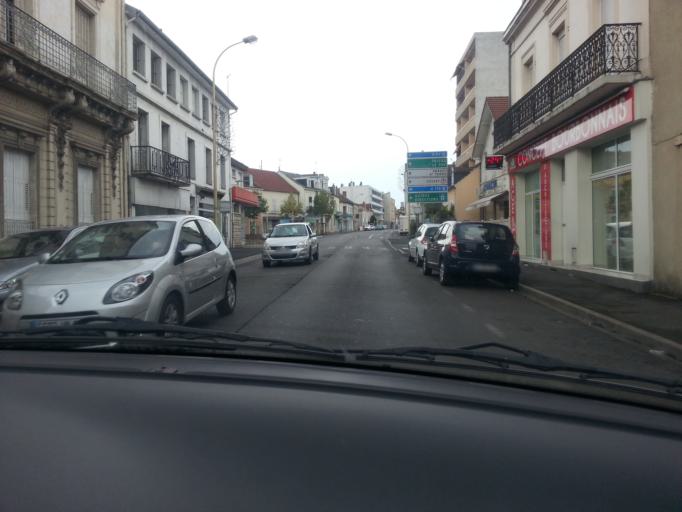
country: FR
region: Auvergne
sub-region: Departement de l'Allier
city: Vichy
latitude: 46.1297
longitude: 3.4319
